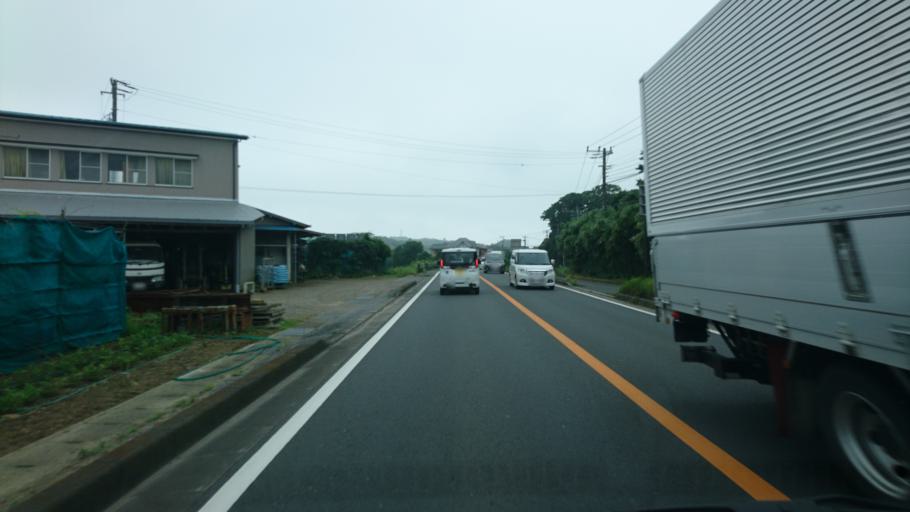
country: JP
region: Chiba
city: Kimitsu
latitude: 35.2657
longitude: 139.8919
